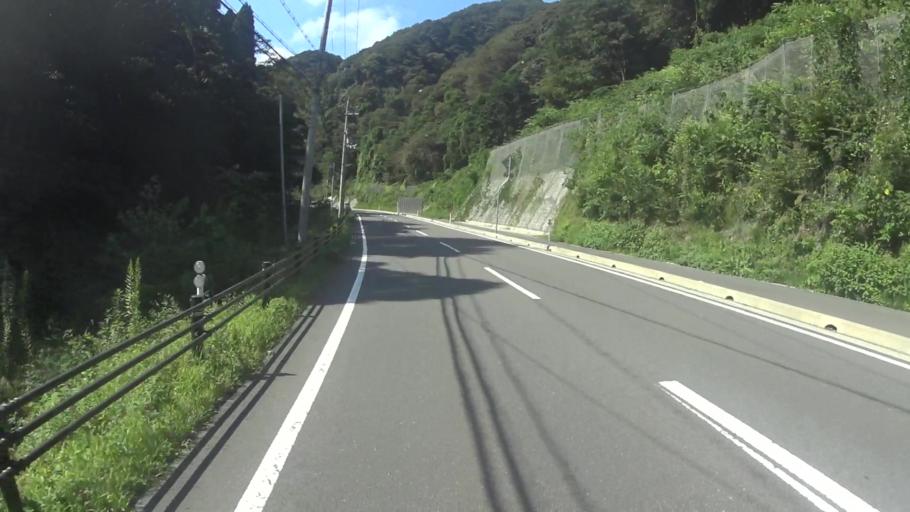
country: JP
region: Kyoto
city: Miyazu
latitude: 35.6864
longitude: 135.2895
